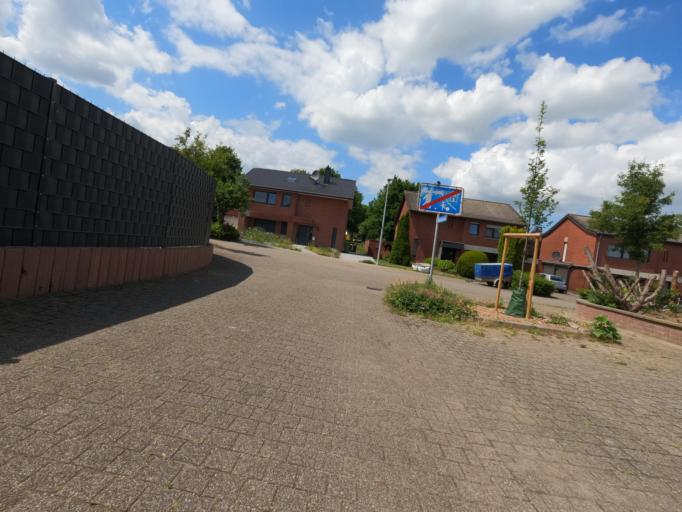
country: DE
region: North Rhine-Westphalia
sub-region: Regierungsbezirk Koln
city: Ubach-Palenberg
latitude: 50.9182
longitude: 6.1116
